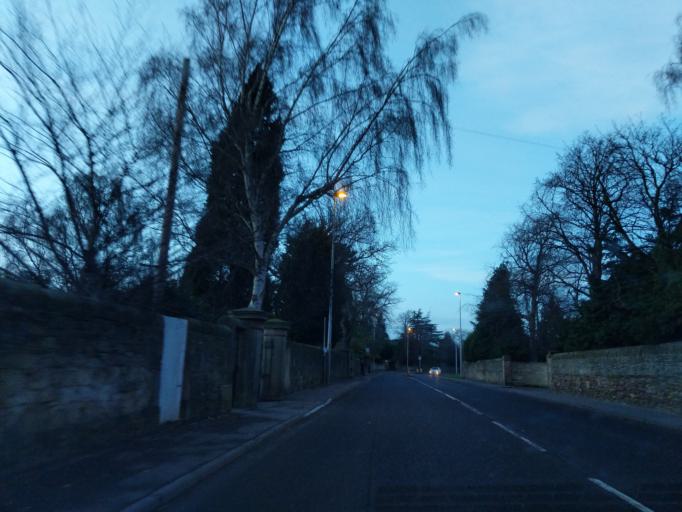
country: GB
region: Scotland
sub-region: Midlothian
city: Bonnyrigg
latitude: 55.8799
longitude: -3.1093
